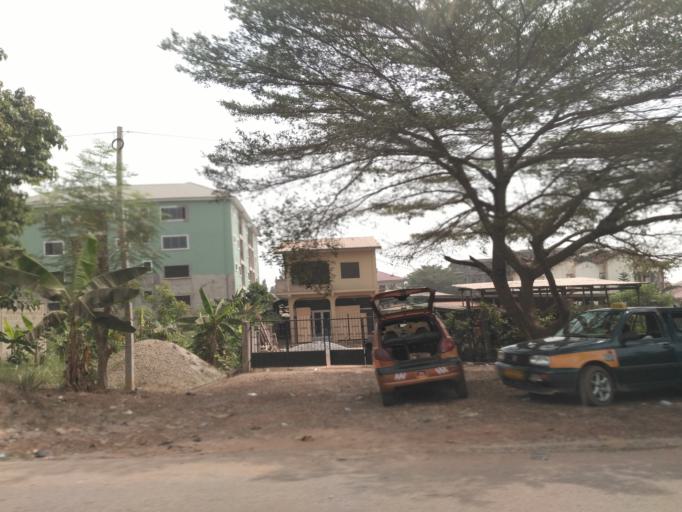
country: GH
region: Ashanti
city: Kumasi
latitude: 6.6465
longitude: -1.6440
